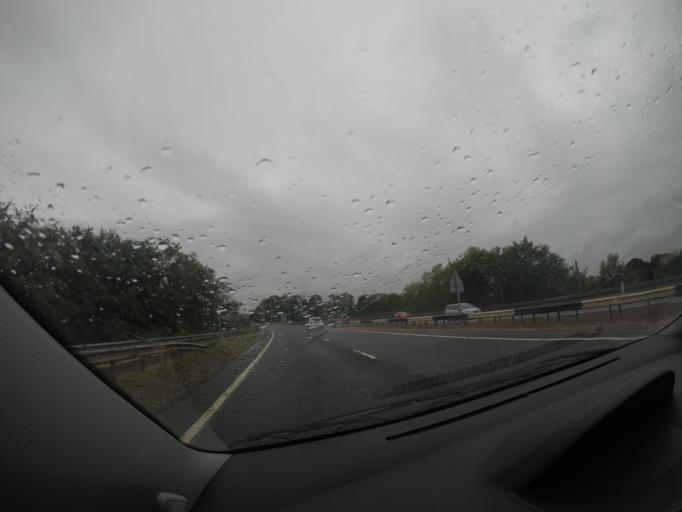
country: GB
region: Scotland
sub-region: Angus
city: Forfar
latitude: 56.7047
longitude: -2.8284
